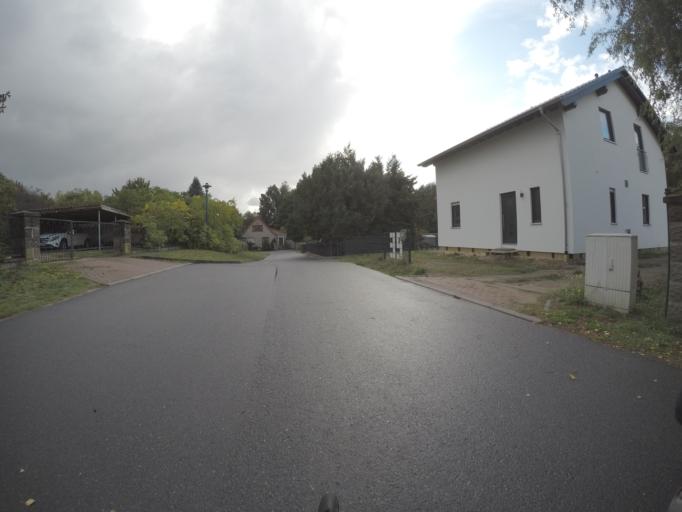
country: DE
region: Brandenburg
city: Wandlitz
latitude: 52.7087
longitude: 13.4349
